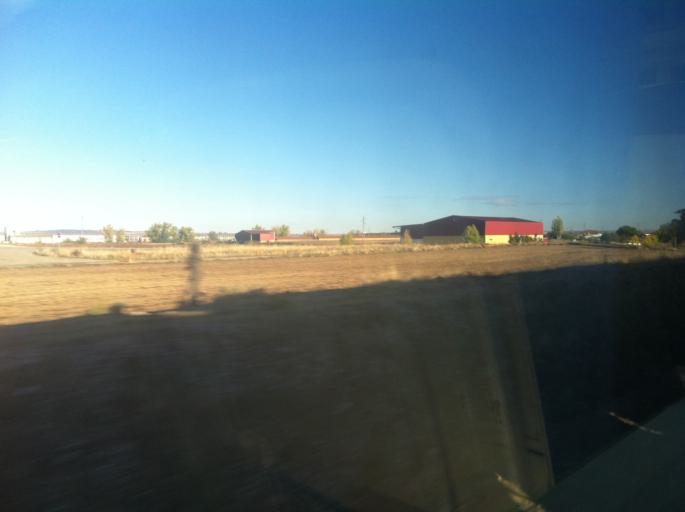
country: ES
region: Castille and Leon
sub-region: Provincia de Valladolid
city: Cabezon
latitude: 41.7479
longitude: -4.6412
